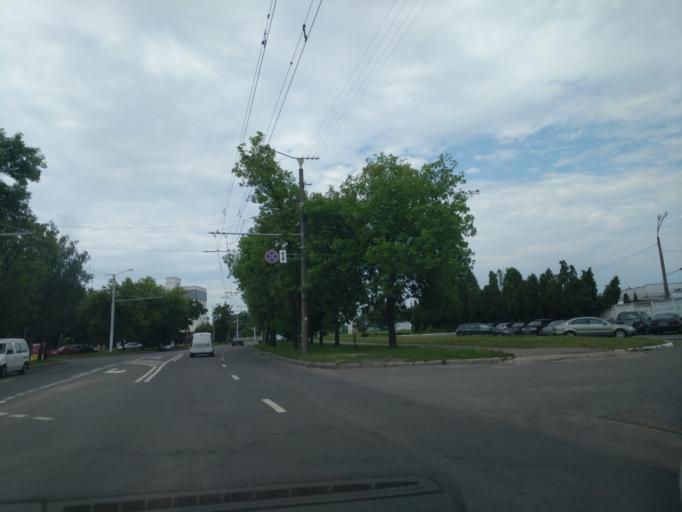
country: BY
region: Minsk
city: Novoye Medvezhino
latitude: 53.8831
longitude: 27.4823
